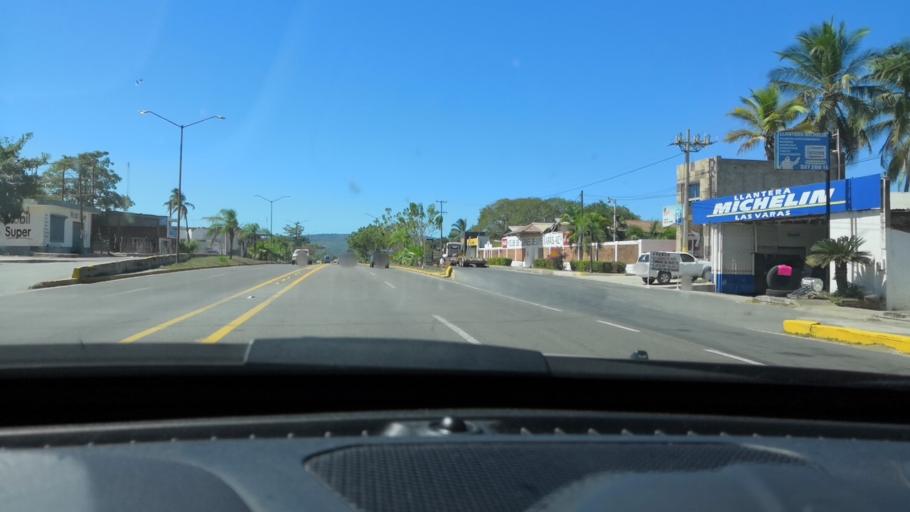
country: MX
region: Nayarit
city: Las Varas
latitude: 21.1848
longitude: -105.1276
